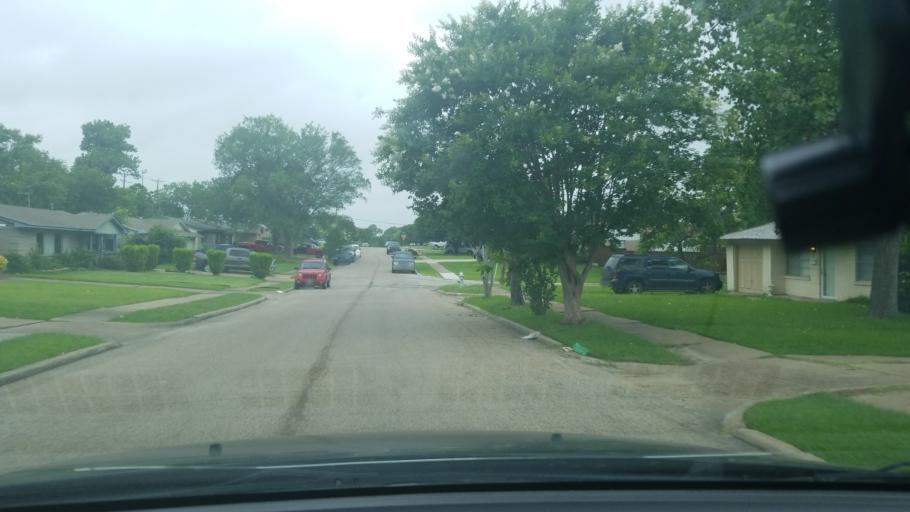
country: US
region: Texas
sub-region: Dallas County
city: Mesquite
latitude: 32.7842
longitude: -96.6356
